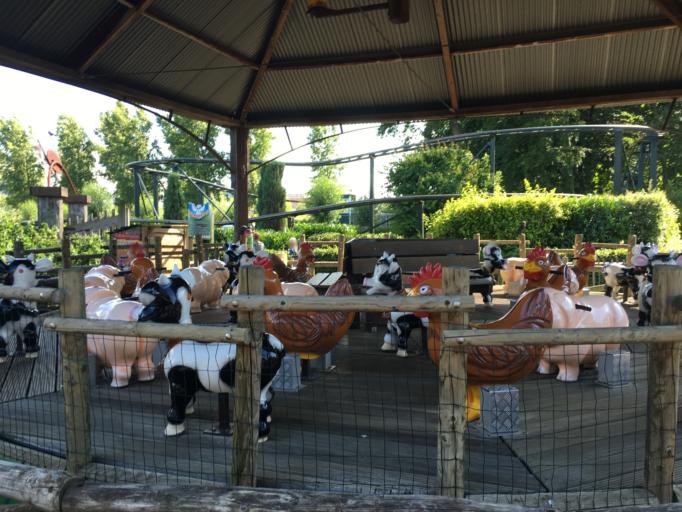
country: NL
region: South Holland
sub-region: Gemeente Leidschendam-Voorburg
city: Voorburg
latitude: 52.0541
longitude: 4.3505
